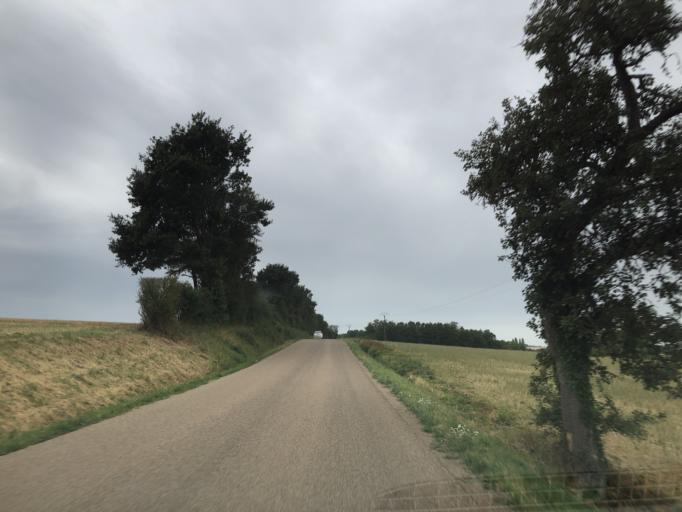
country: FR
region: Bourgogne
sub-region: Departement de l'Yonne
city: Charny
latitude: 47.9504
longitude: 3.1345
